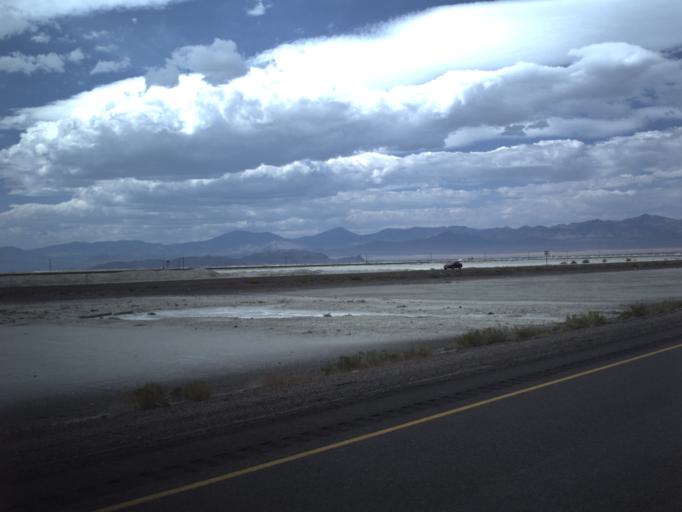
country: US
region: Utah
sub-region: Tooele County
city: Wendover
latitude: 40.7413
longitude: -113.9468
